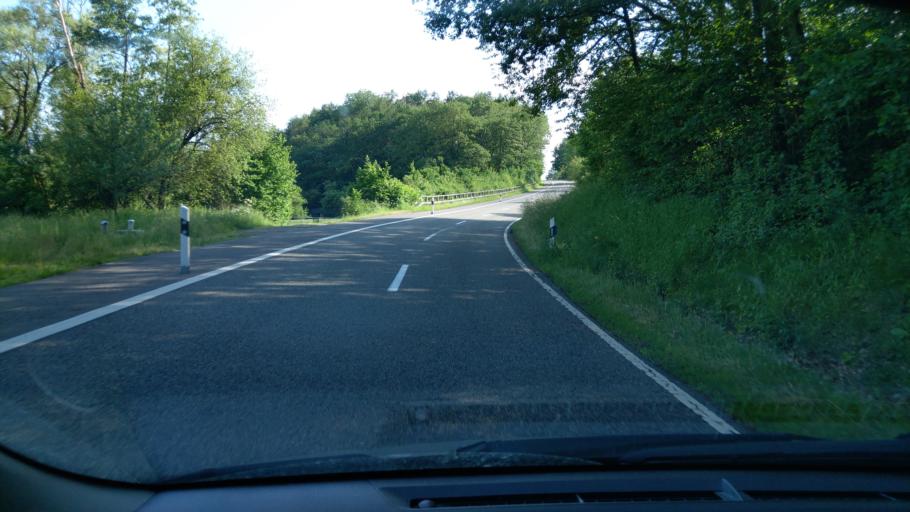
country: DE
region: Saarland
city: Wadern
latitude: 49.4959
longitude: 6.9321
